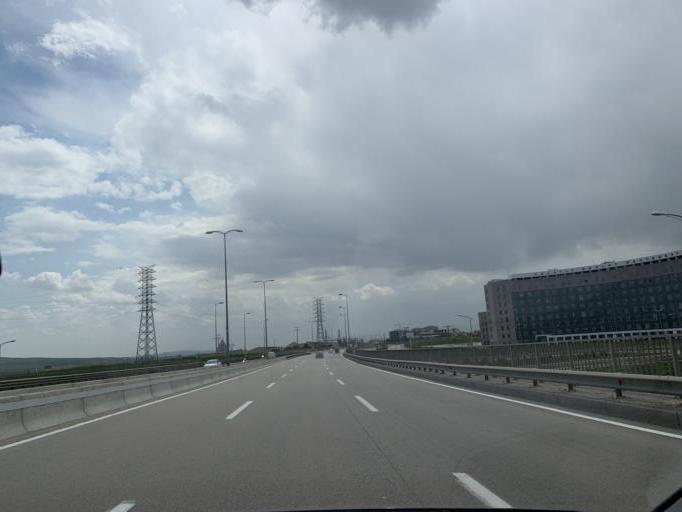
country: TR
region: Ankara
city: Polatli
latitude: 39.5899
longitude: 32.1709
